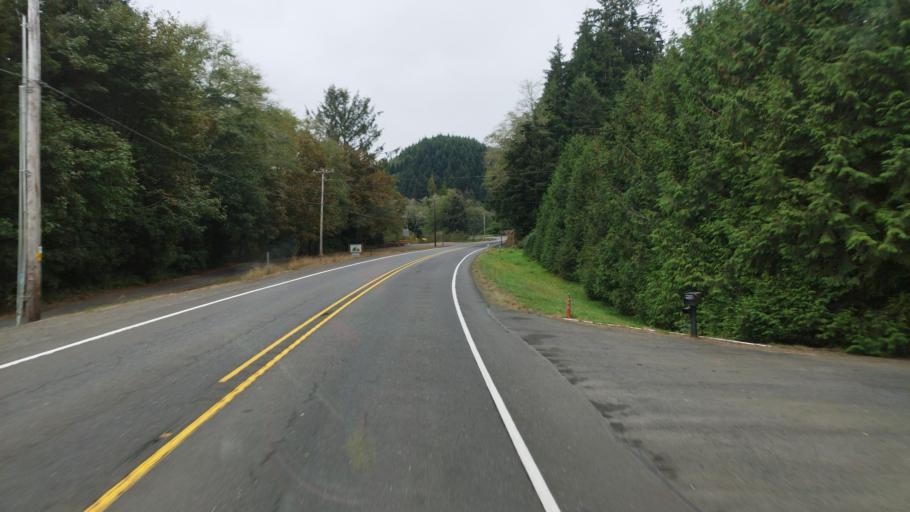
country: US
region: Oregon
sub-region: Clatsop County
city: Cannon Beach
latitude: 45.9227
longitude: -123.8955
